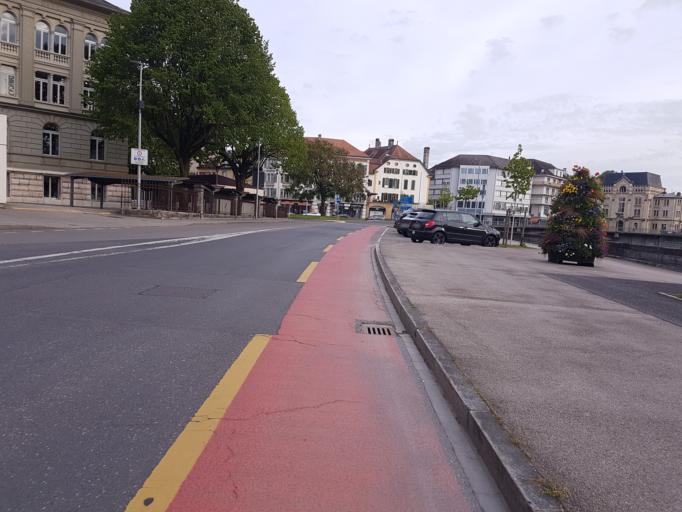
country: CH
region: Vaud
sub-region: Jura-Nord vaudois District
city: Yverdon-les-Bains
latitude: 46.7815
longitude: 6.6380
